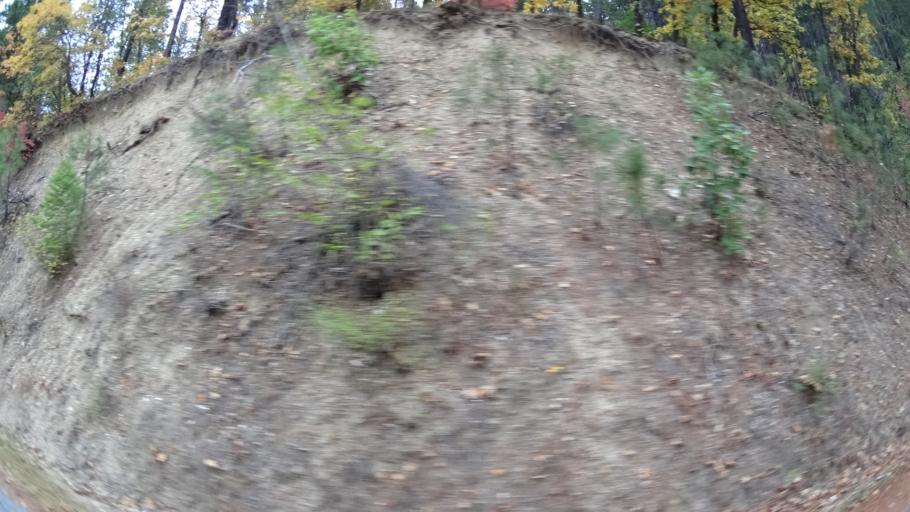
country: US
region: California
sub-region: Siskiyou County
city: Happy Camp
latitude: 41.8282
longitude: -123.1808
